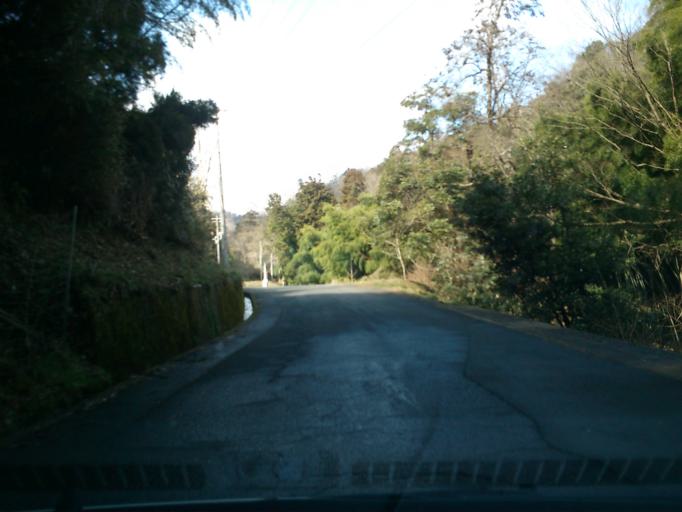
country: JP
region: Kyoto
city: Miyazu
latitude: 35.5811
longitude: 135.1773
